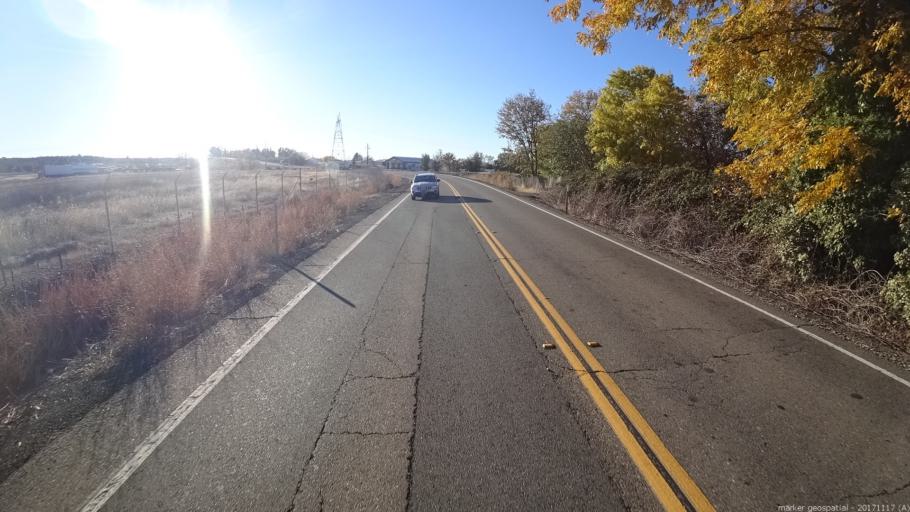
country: US
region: California
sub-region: Shasta County
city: Anderson
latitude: 40.4413
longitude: -122.2810
